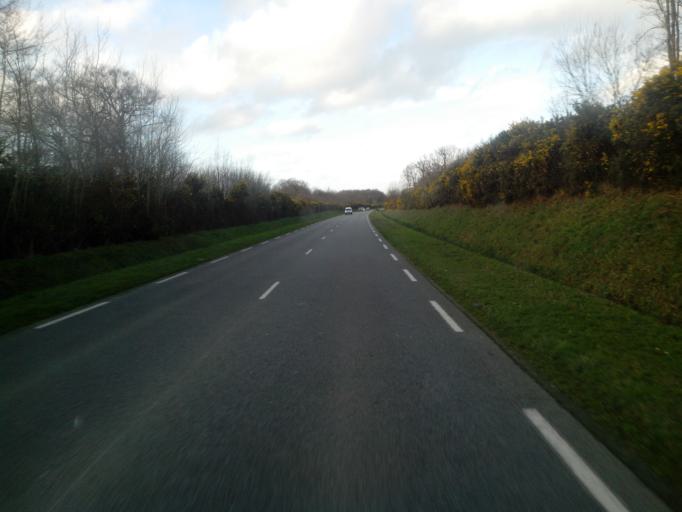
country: FR
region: Brittany
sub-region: Departement des Cotes-d'Armor
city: Pleslin-Trigavou
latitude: 48.5509
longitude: -2.0459
